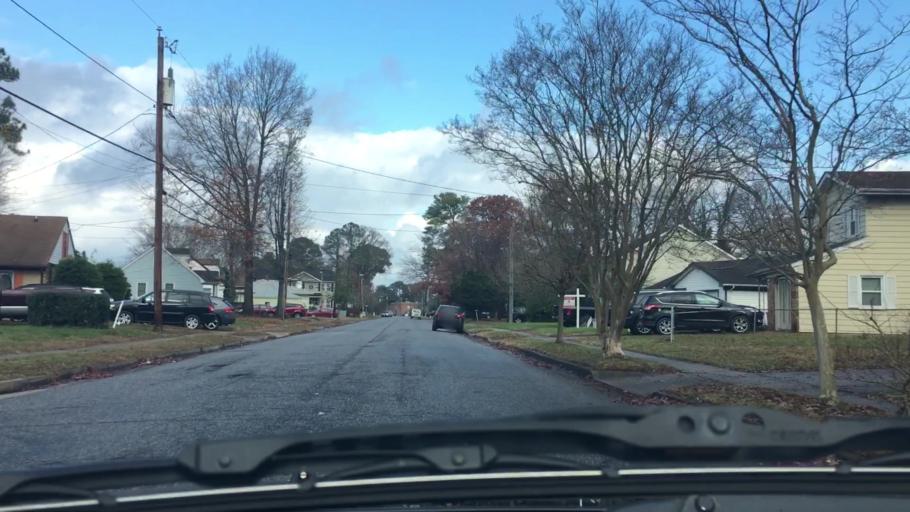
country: US
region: Virginia
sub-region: City of Norfolk
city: Norfolk
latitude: 36.9247
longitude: -76.2459
